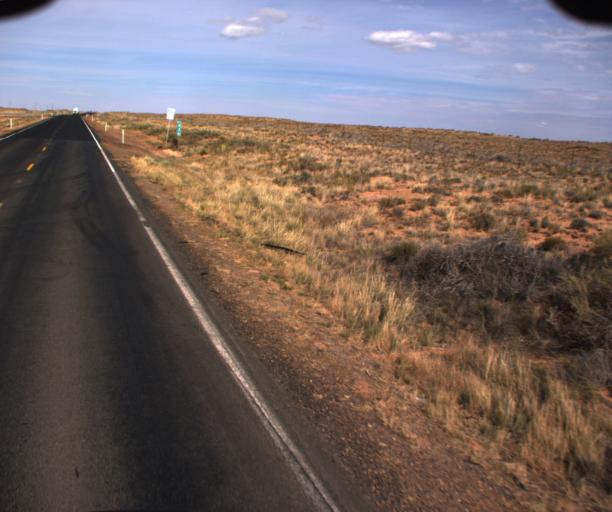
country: US
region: Arizona
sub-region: Apache County
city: Chinle
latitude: 36.0124
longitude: -109.6047
